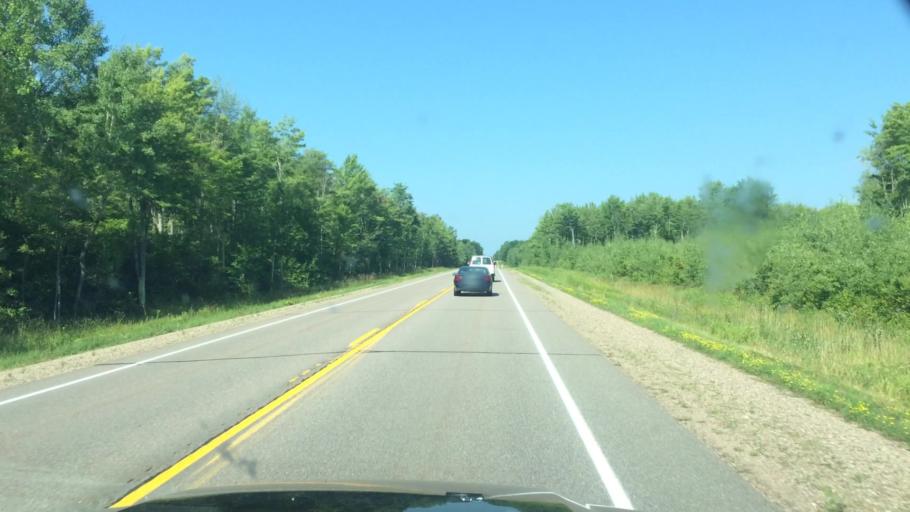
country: US
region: Wisconsin
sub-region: Langlade County
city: Antigo
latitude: 45.1469
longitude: -89.3723
